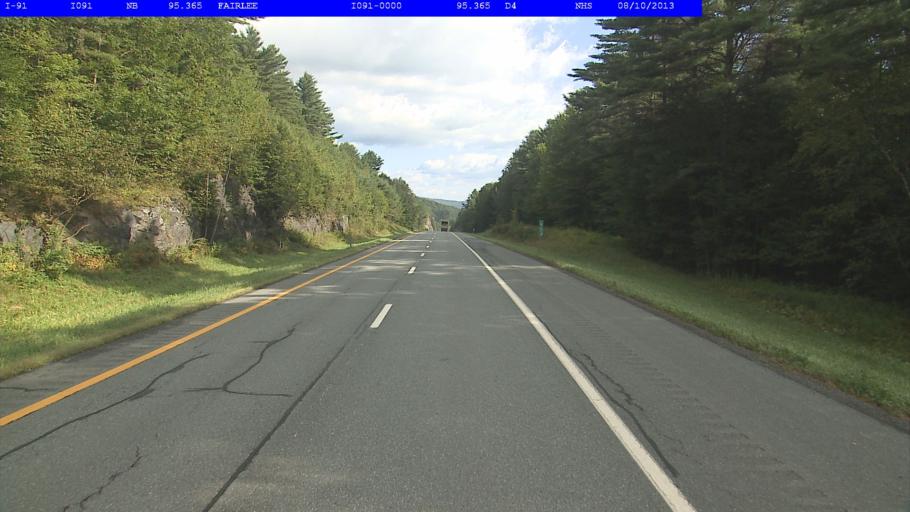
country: US
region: New Hampshire
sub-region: Grafton County
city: Orford
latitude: 43.9525
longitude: -72.1298
